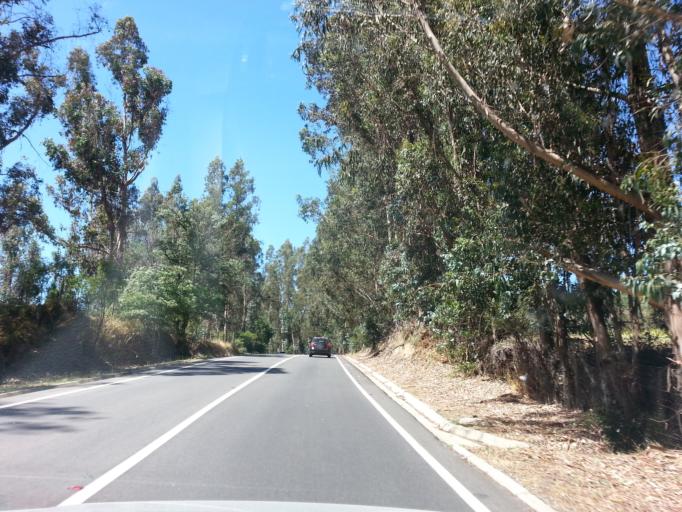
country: CL
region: Valparaiso
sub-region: Provincia de Marga Marga
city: Villa Alemana
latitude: -33.1906
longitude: -71.3707
